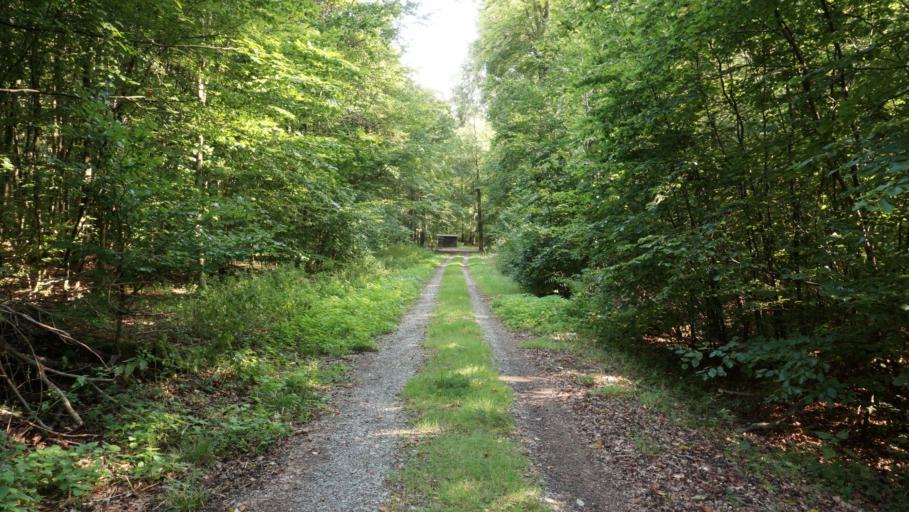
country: DE
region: Baden-Wuerttemberg
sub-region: Karlsruhe Region
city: Neckarzimmern
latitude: 49.3331
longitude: 9.1346
